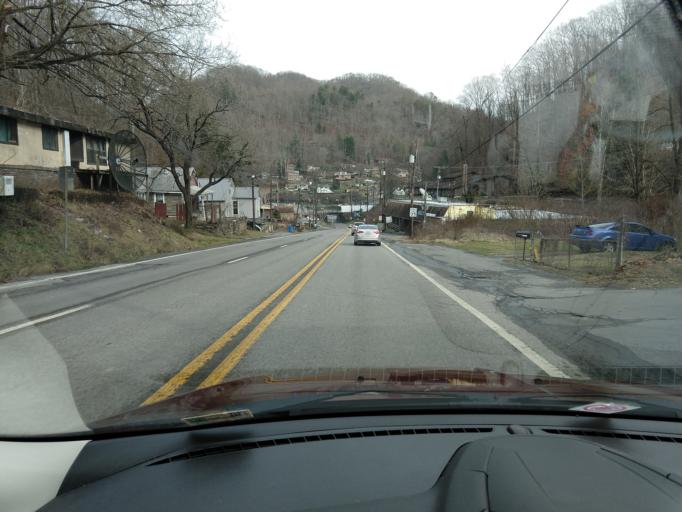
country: US
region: West Virginia
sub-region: McDowell County
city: Welch
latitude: 37.4157
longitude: -81.5945
